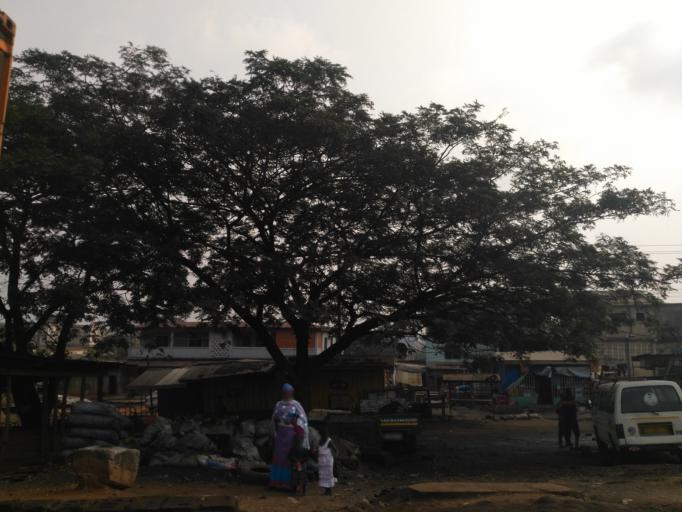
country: GH
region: Ashanti
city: Kumasi
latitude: 6.6963
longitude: -1.5929
